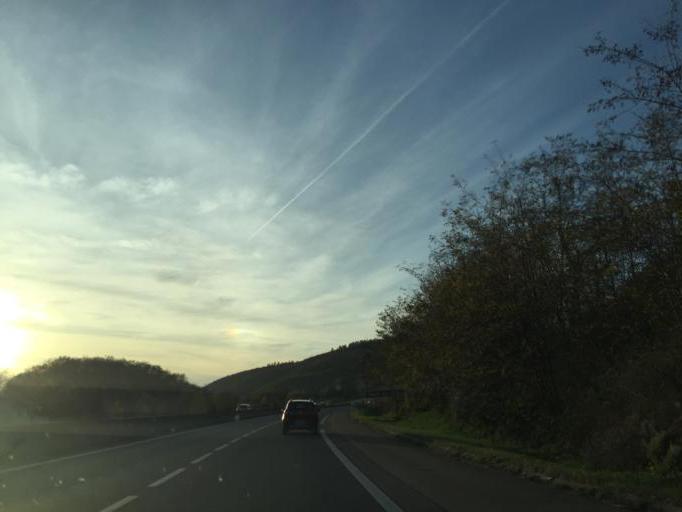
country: FR
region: Rhone-Alpes
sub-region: Departement du Rhone
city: Chassagny
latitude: 45.5792
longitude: 4.7337
